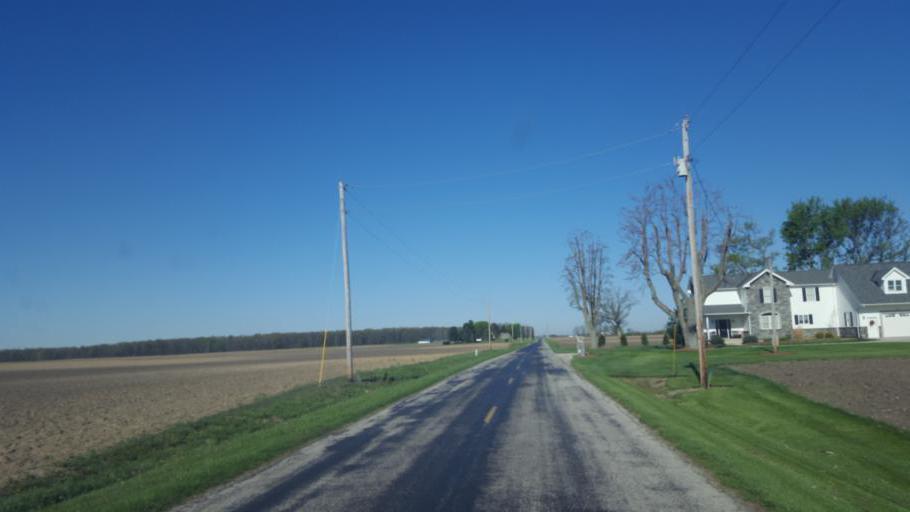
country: US
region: Ohio
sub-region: Marion County
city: Marion
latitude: 40.6884
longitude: -83.0732
